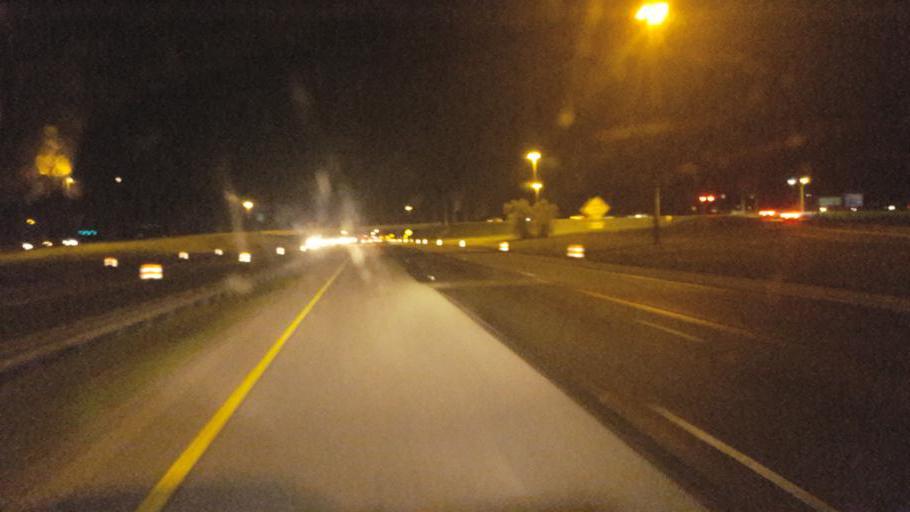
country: US
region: Indiana
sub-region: Hendricks County
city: Plainfield
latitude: 39.6693
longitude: -86.3675
